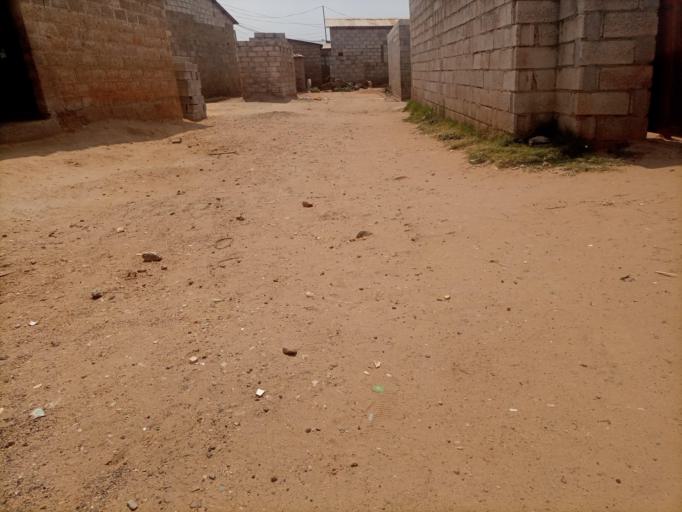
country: ZM
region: Lusaka
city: Lusaka
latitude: -15.4050
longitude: 28.3732
